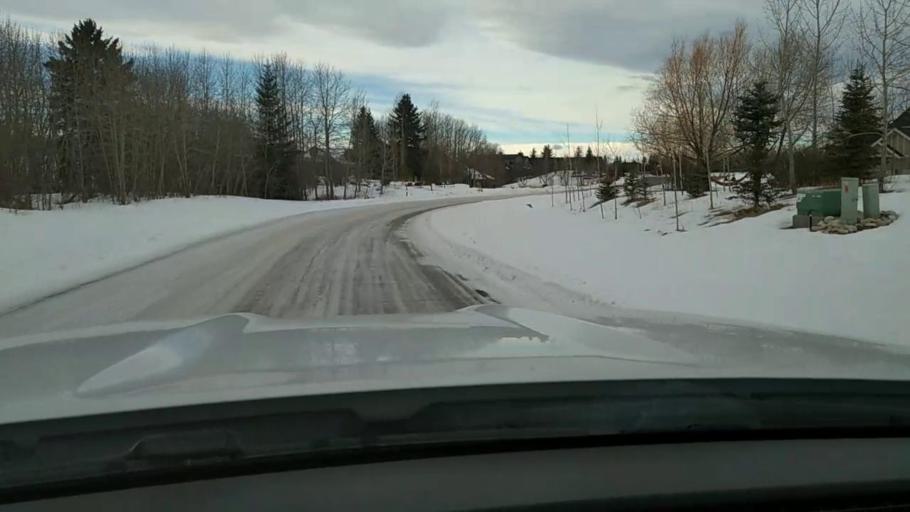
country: CA
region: Alberta
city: Cochrane
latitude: 51.1849
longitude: -114.2593
